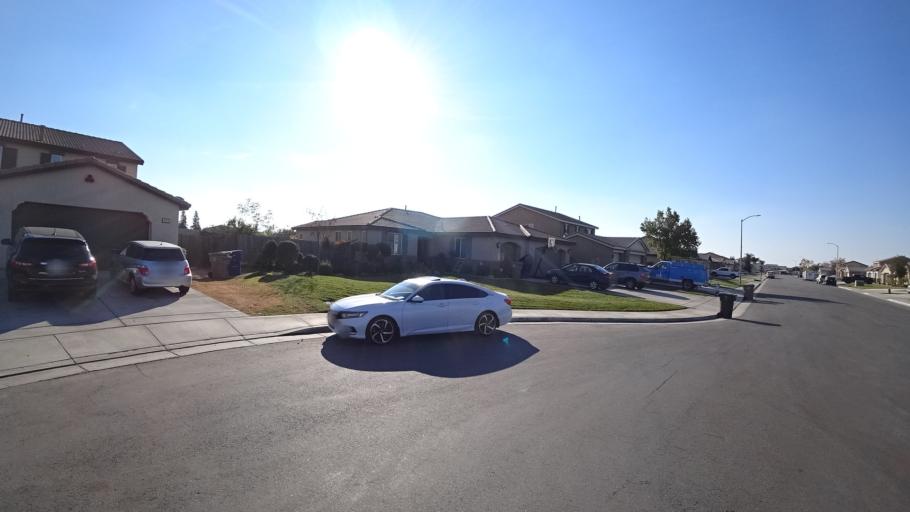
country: US
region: California
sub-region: Kern County
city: Greenfield
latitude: 35.2827
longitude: -119.0527
